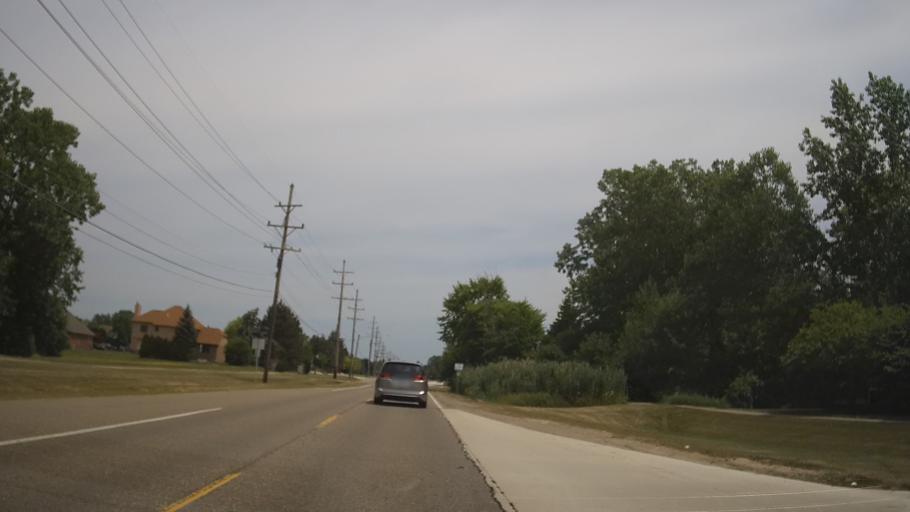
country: US
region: Michigan
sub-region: Macomb County
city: Utica
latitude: 42.6079
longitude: -83.0788
